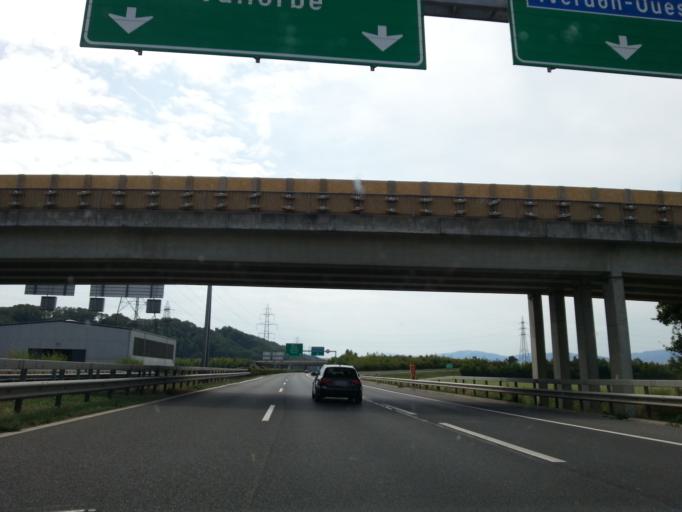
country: CH
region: Vaud
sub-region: Jura-Nord vaudois District
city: Yverdon-les-Bains
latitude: 46.7606
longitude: 6.6408
